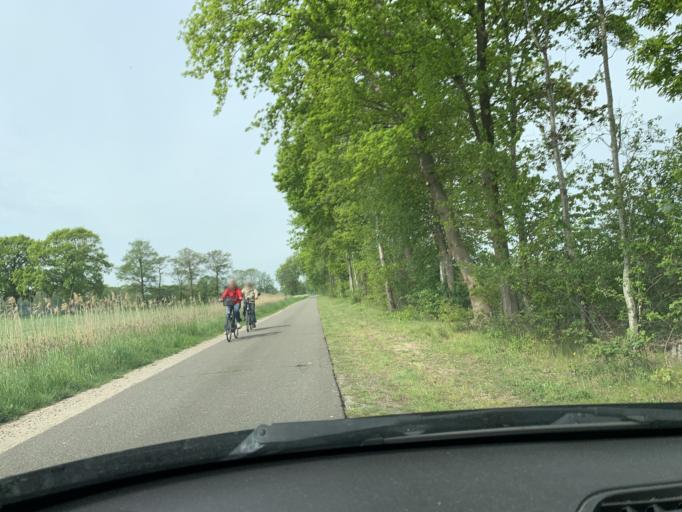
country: DE
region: Lower Saxony
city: Apen
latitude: 53.2129
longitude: 7.7892
